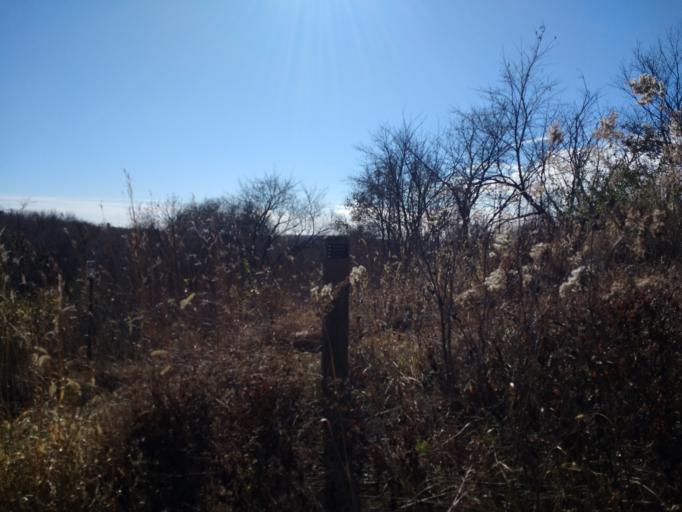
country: US
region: South Dakota
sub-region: Union County
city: North Sioux City
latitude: 42.5413
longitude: -96.4665
